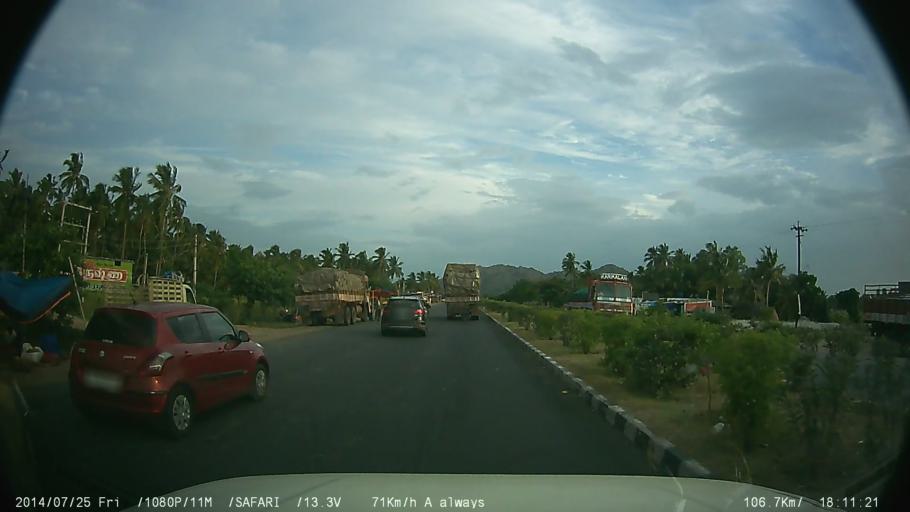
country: IN
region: Tamil Nadu
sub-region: Krishnagiri
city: Kaverippattanam
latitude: 12.3638
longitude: 78.2145
